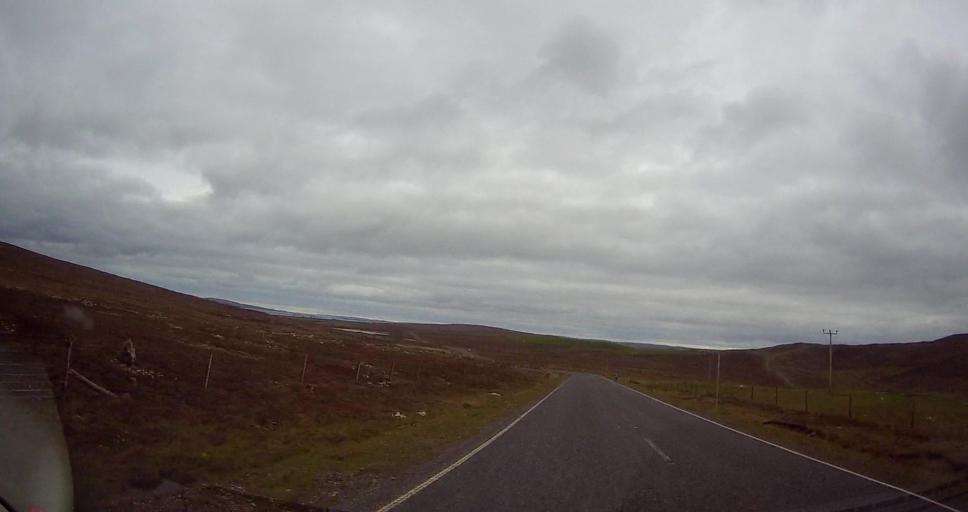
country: GB
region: Scotland
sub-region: Shetland Islands
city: Shetland
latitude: 60.7247
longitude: -0.9059
